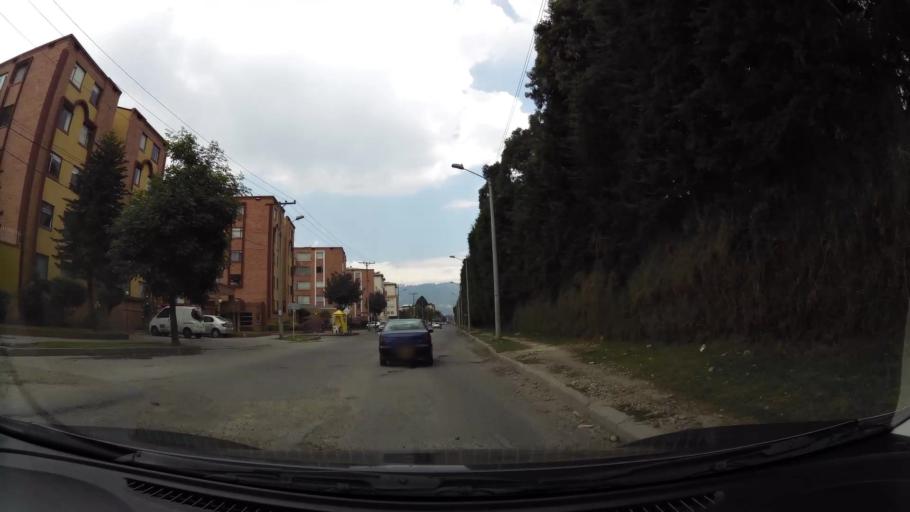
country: CO
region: Cundinamarca
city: Cota
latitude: 4.7460
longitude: -74.0529
